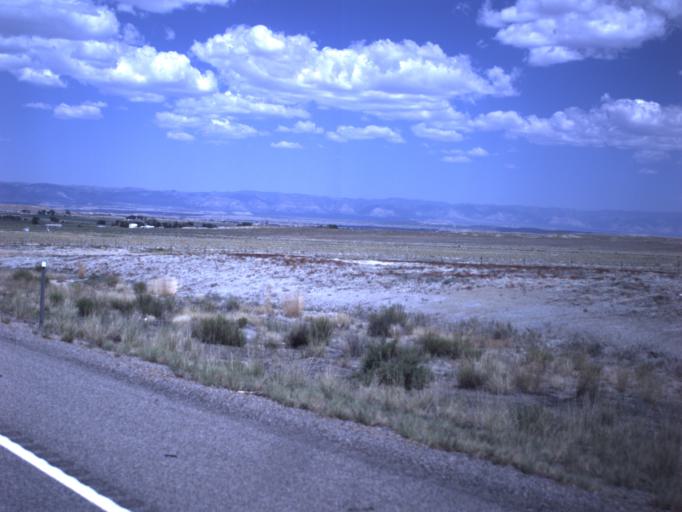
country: US
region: Utah
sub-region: Carbon County
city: Price
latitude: 39.5052
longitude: -110.8371
